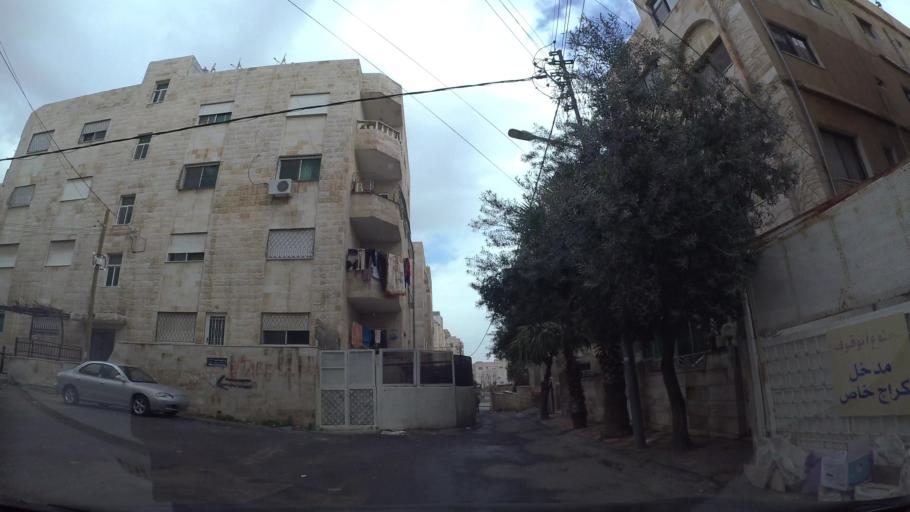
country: JO
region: Amman
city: Amman
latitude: 31.9870
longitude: 35.9250
